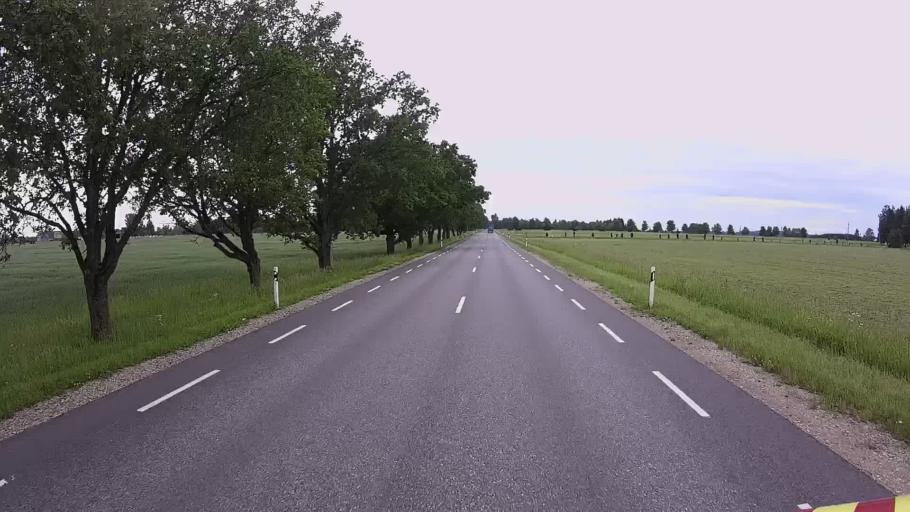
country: EE
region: Viljandimaa
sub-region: Karksi vald
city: Karksi-Nuia
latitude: 58.1298
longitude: 25.5826
